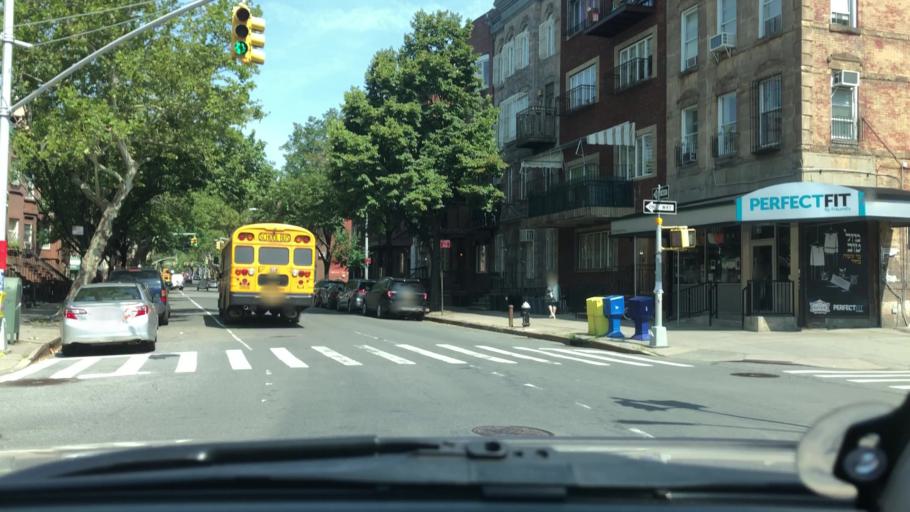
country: US
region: New York
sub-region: Queens County
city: Long Island City
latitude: 40.7008
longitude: -73.9574
